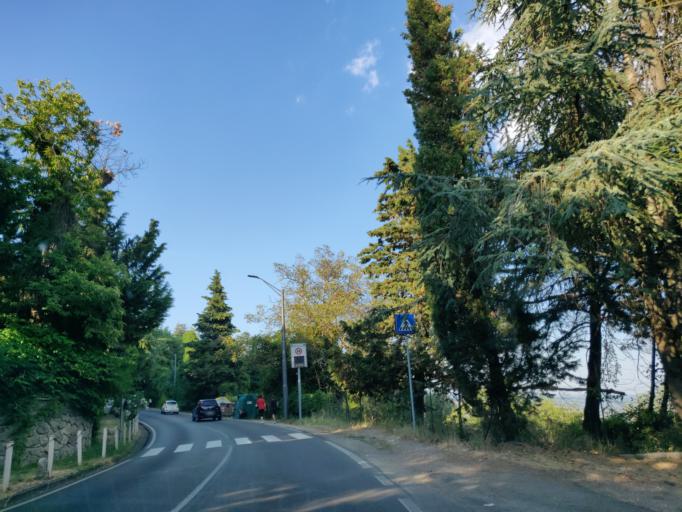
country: IT
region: Tuscany
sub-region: Provincia di Siena
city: Abbadia San Salvatore
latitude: 42.8743
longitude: 11.6837
